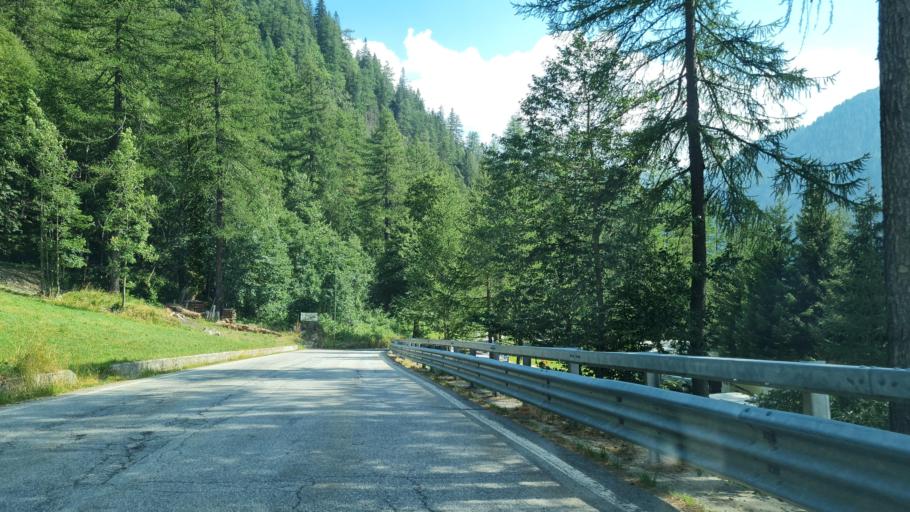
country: IT
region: Piedmont
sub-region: Provincia Verbano-Cusio-Ossola
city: Formazza
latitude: 46.3845
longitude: 8.4254
